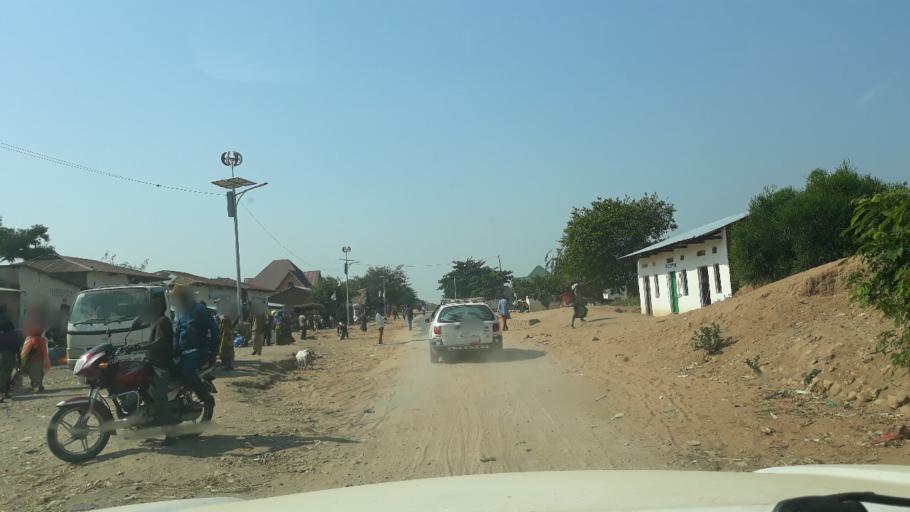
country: CD
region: South Kivu
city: Uvira
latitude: -3.2377
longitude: 29.1628
